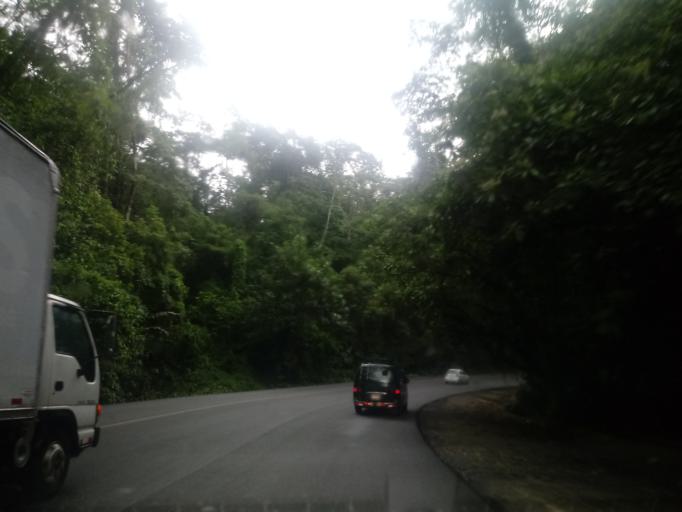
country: CR
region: San Jose
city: Dulce Nombre de Jesus
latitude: 10.1467
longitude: -83.9544
